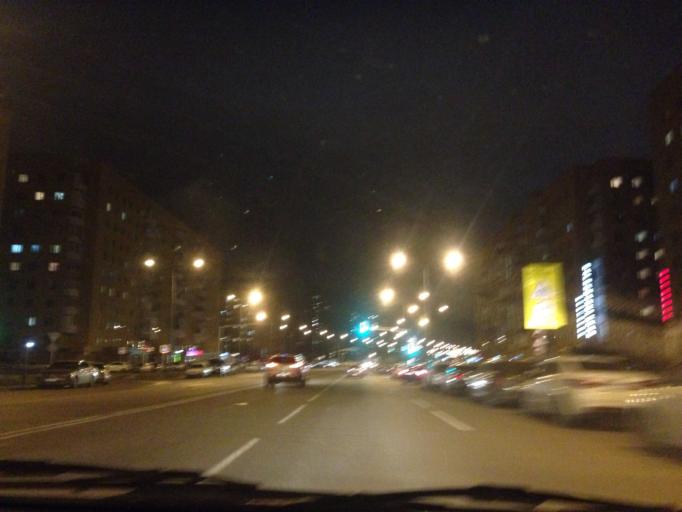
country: KZ
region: Astana Qalasy
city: Astana
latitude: 51.1711
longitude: 71.3837
